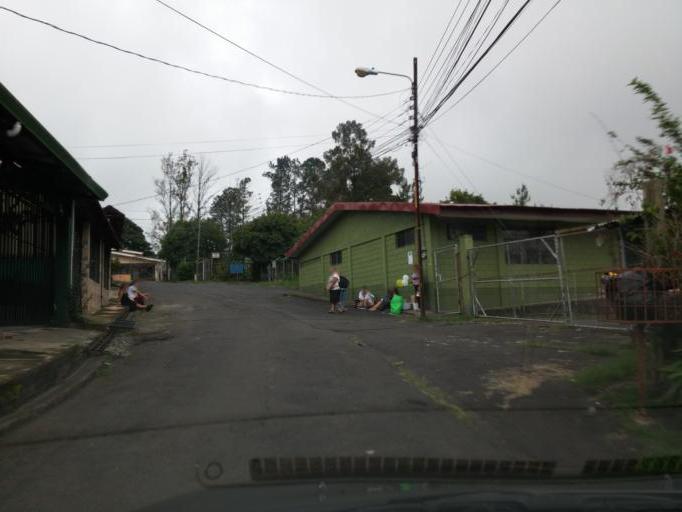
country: CR
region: Heredia
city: San Josecito
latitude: 10.0395
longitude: -84.1070
